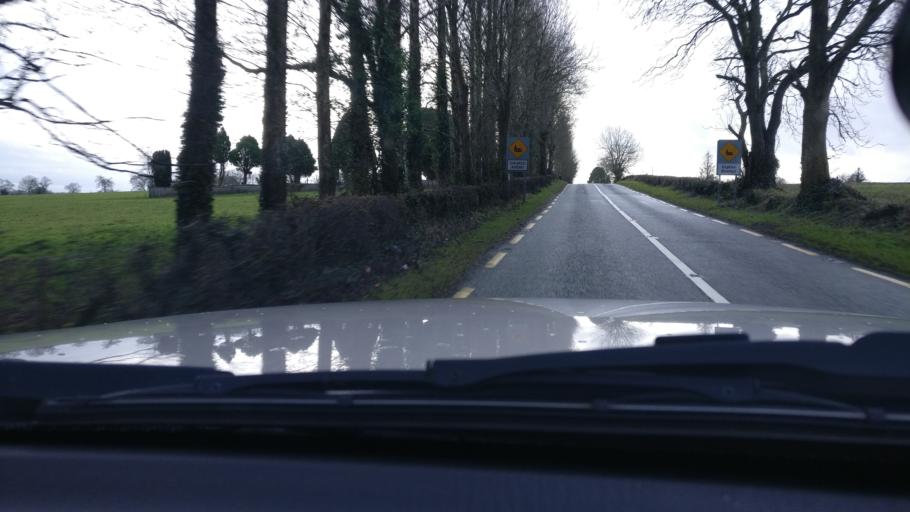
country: IE
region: Leinster
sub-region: An Iarmhi
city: Moate
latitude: 53.6057
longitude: -7.7110
